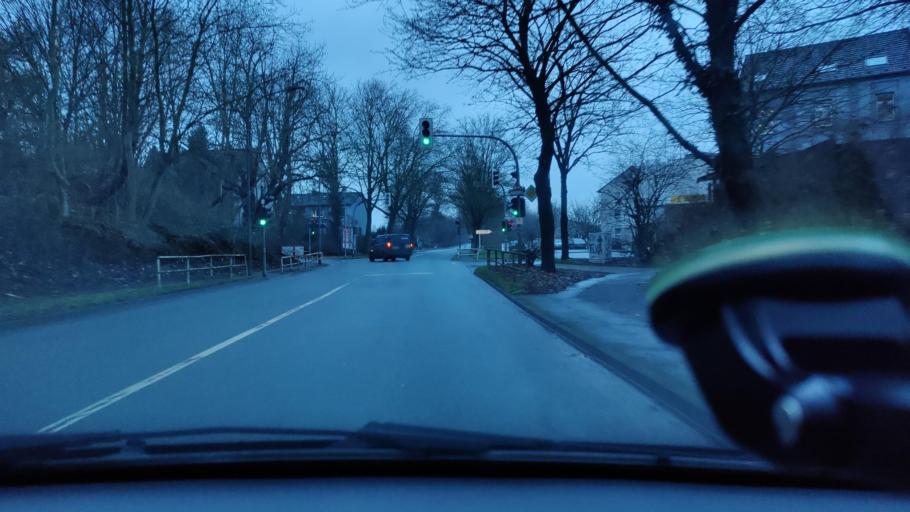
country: DE
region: North Rhine-Westphalia
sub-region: Regierungsbezirk Arnsberg
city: Bochum
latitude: 51.4827
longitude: 7.2863
